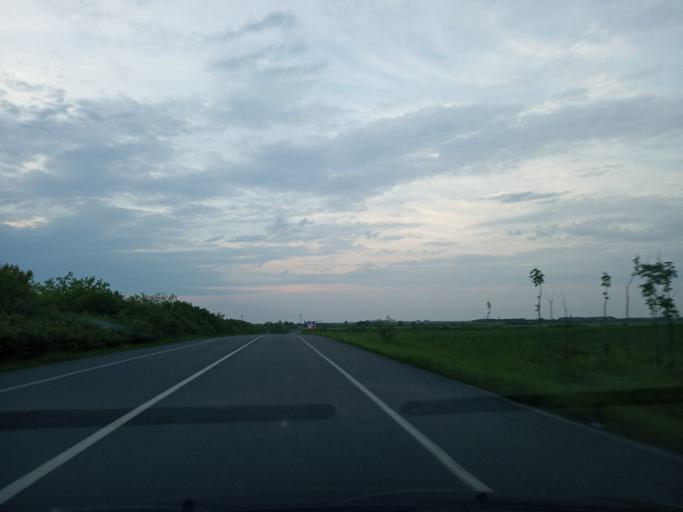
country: RO
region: Timis
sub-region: Oras Deta
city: Deta
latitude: 45.4120
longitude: 21.2298
